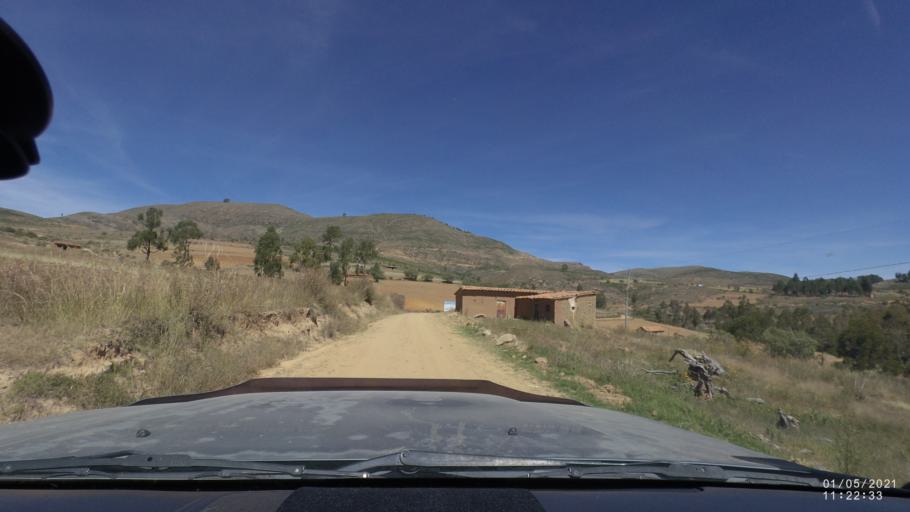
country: BO
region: Cochabamba
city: Tarata
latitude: -17.6499
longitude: -66.1317
